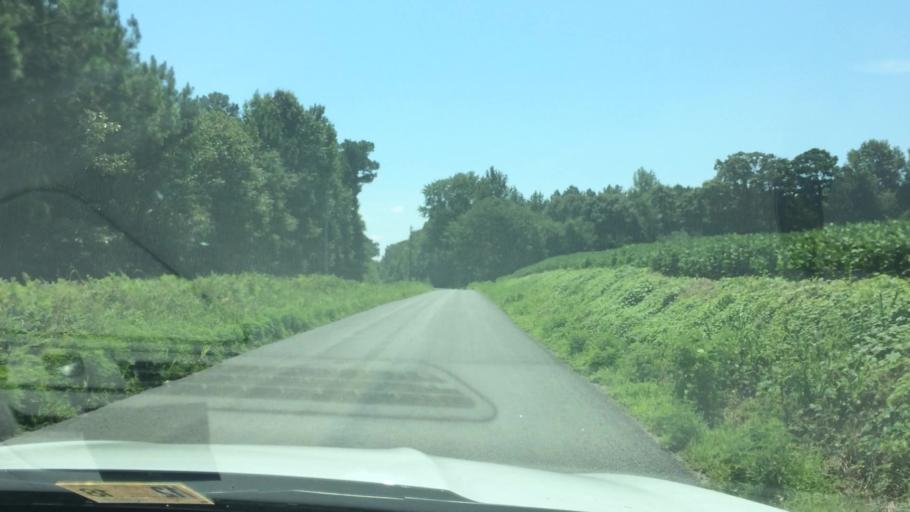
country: US
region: Virginia
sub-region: Charles City County
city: Charles City
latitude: 37.3039
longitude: -76.9656
